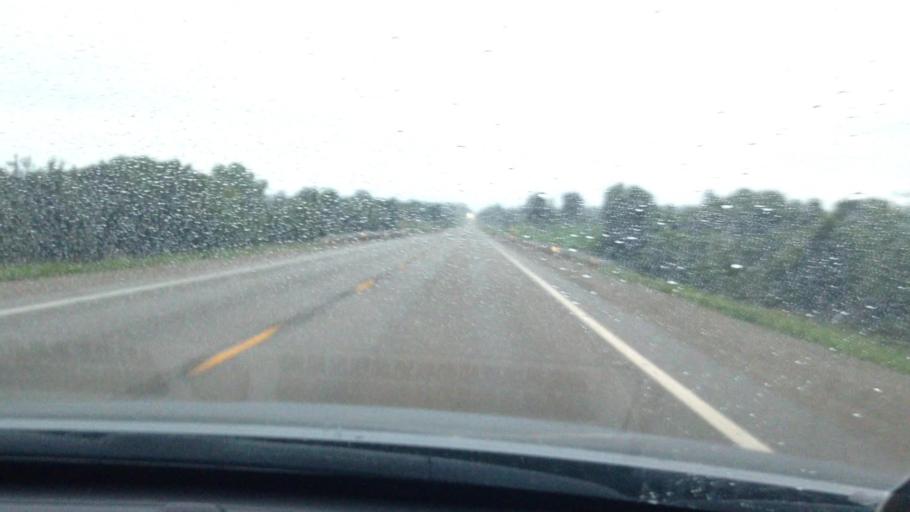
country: US
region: Kansas
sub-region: Brown County
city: Hiawatha
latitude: 39.8337
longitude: -95.5271
